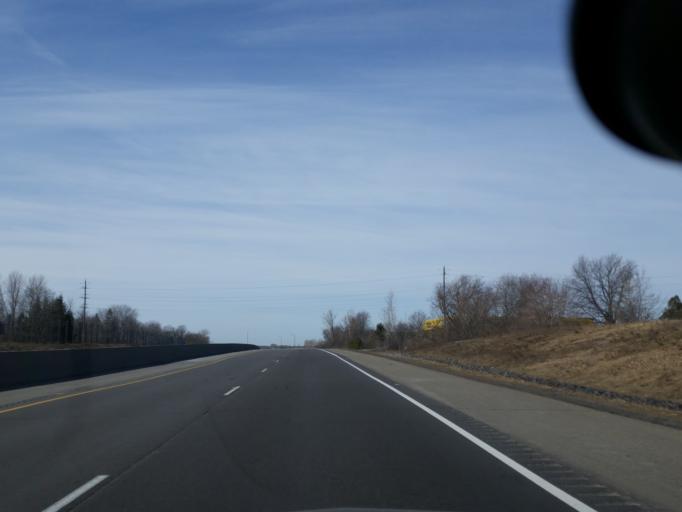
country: CA
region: Ontario
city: Brockville
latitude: 44.6174
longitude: -75.6768
